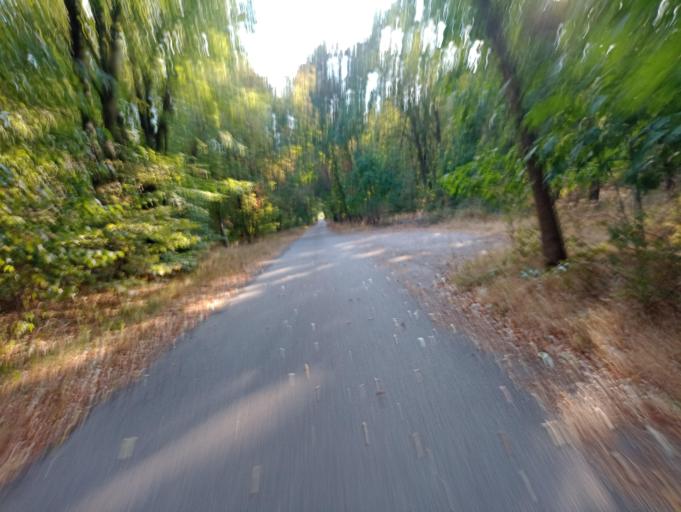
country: DE
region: Hesse
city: Niederrad
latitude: 50.0607
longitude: 8.6185
